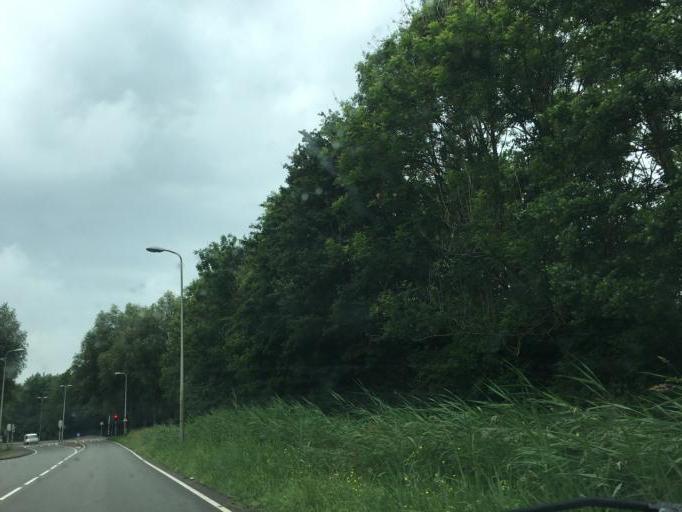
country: NL
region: South Holland
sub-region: Gemeente Capelle aan den IJssel
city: Capelle aan den IJssel
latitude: 51.9499
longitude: 4.5984
